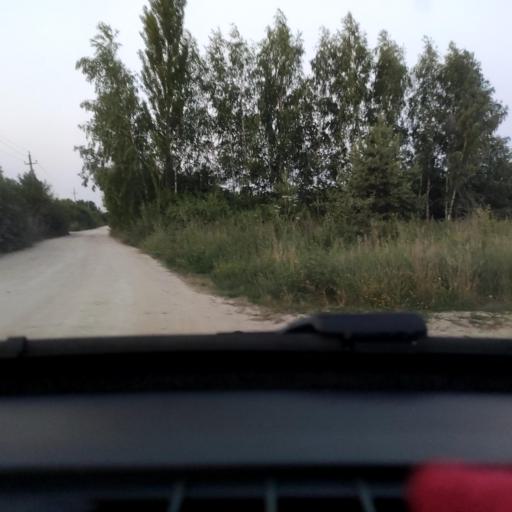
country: RU
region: Voronezj
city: Podgornoye
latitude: 51.8602
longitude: 39.1070
